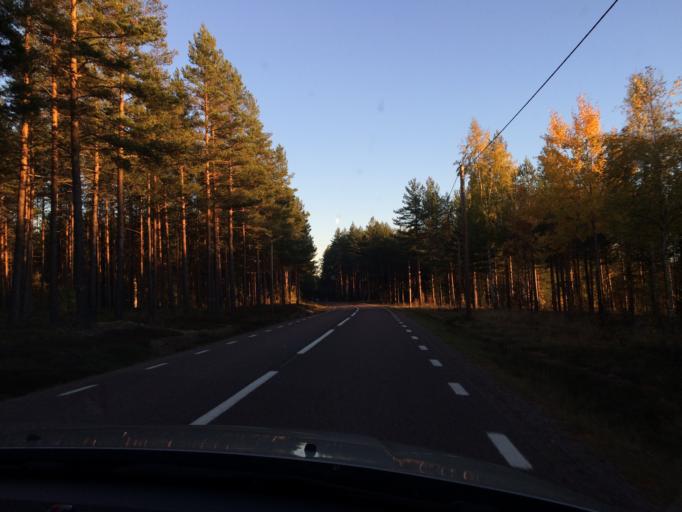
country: SE
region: Gaevleborg
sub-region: Sandvikens Kommun
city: Arsunda
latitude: 60.3798
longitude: 16.7530
